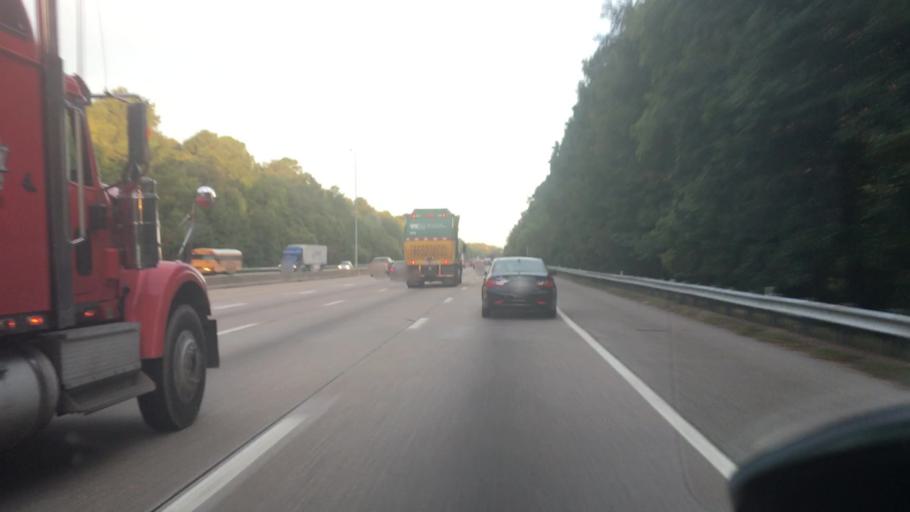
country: US
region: Virginia
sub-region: City of Newport News
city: Newport News
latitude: 37.0684
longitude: -76.4315
